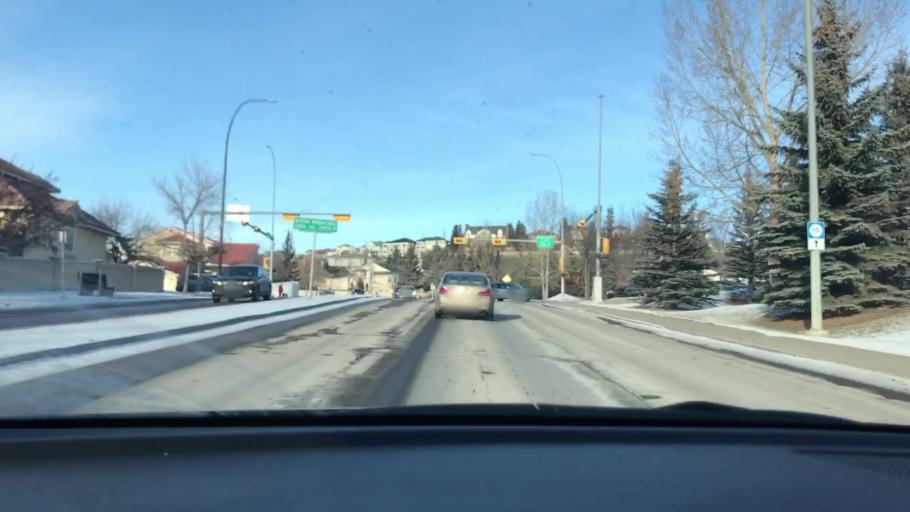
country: CA
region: Alberta
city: Calgary
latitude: 51.0174
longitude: -114.1760
